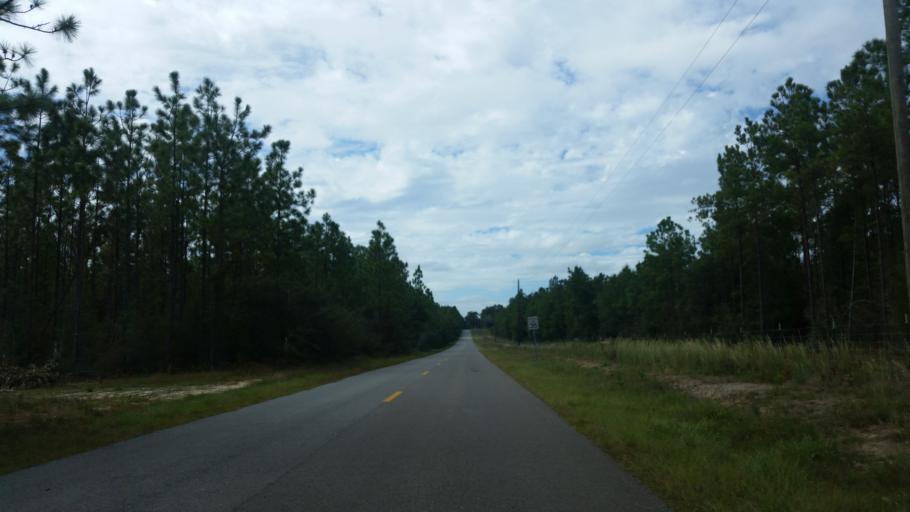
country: US
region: Florida
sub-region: Santa Rosa County
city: Point Baker
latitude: 30.7323
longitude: -87.0029
